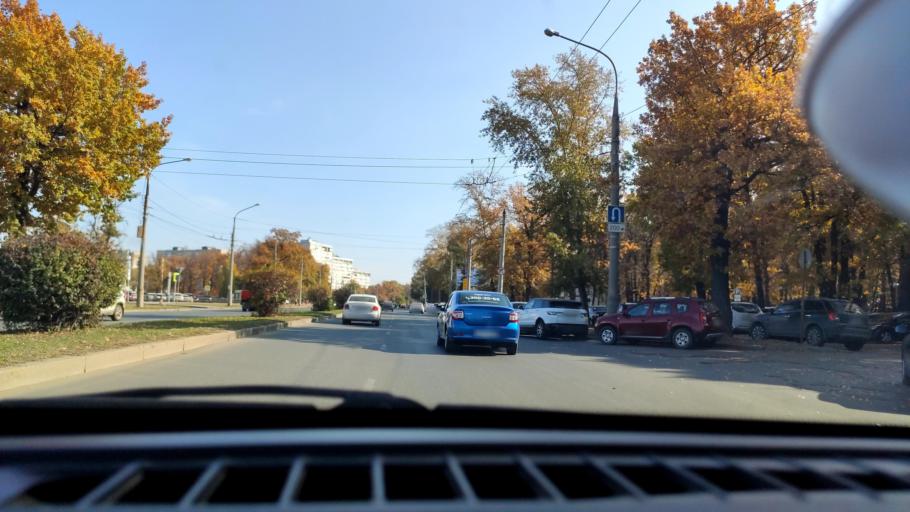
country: RU
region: Samara
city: Samara
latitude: 53.2324
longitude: 50.1987
